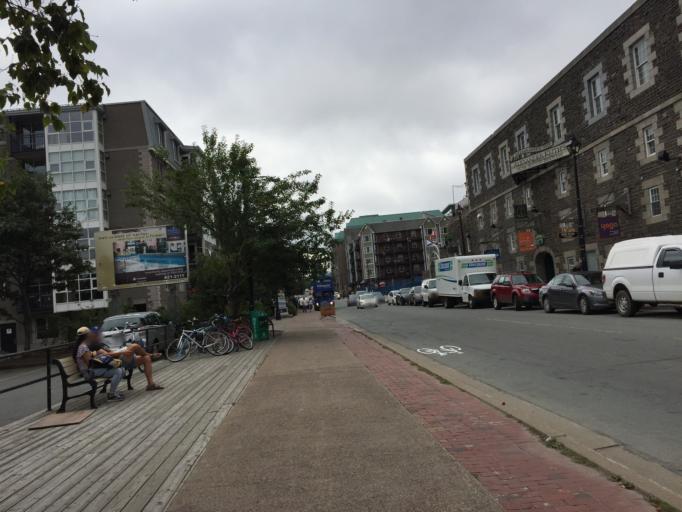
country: CA
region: Nova Scotia
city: Halifax
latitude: 44.6448
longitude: -63.5701
